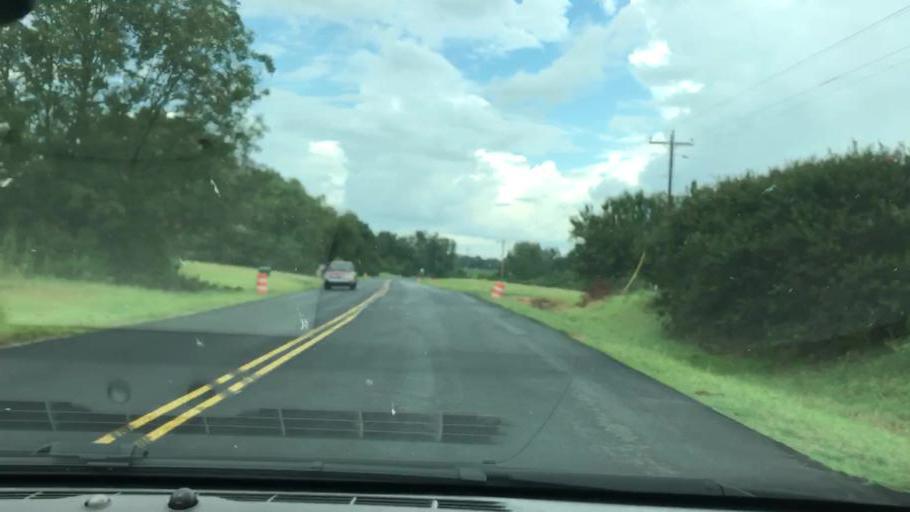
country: US
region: Georgia
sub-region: Early County
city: Blakely
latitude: 31.4222
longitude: -84.9644
